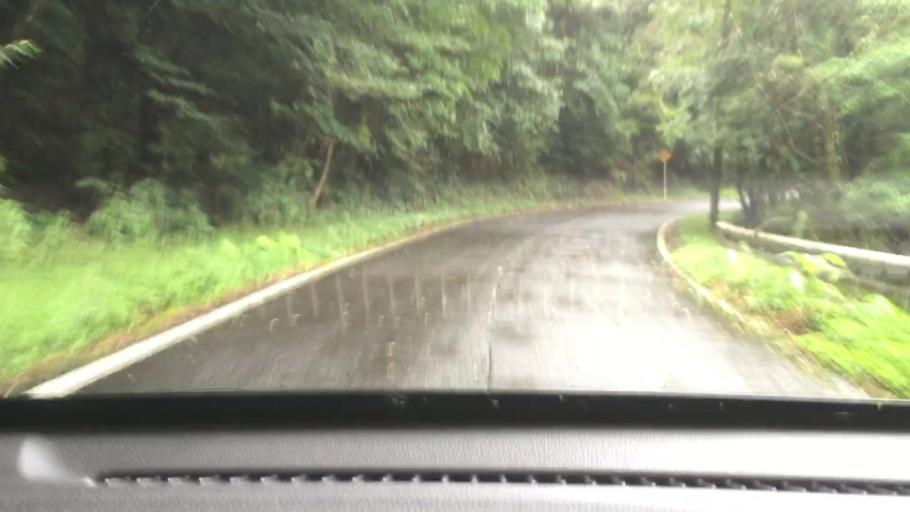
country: JP
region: Nagasaki
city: Togitsu
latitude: 32.9535
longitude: 129.7364
